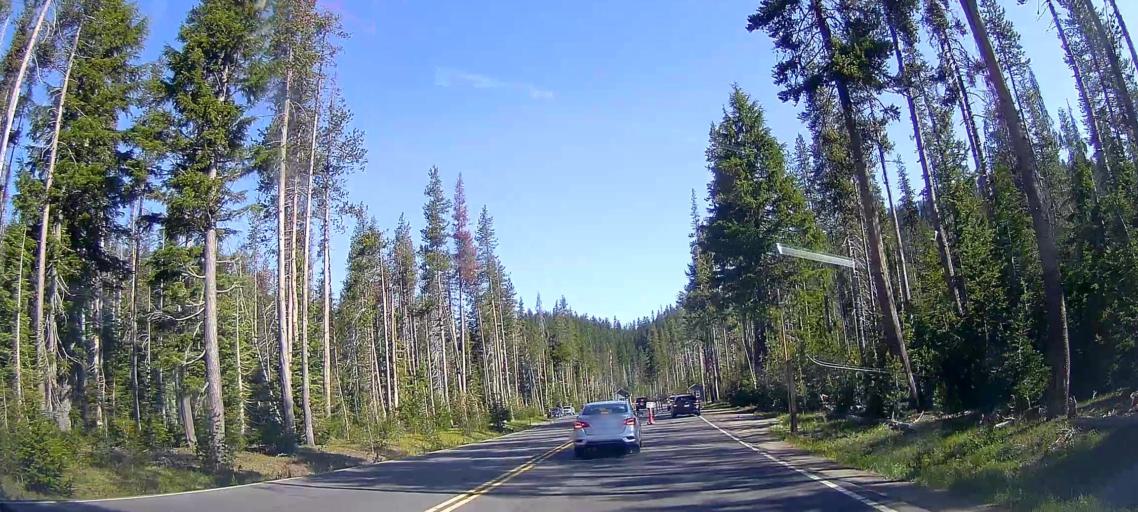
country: US
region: Oregon
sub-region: Jackson County
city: Shady Cove
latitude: 42.8679
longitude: -122.1687
